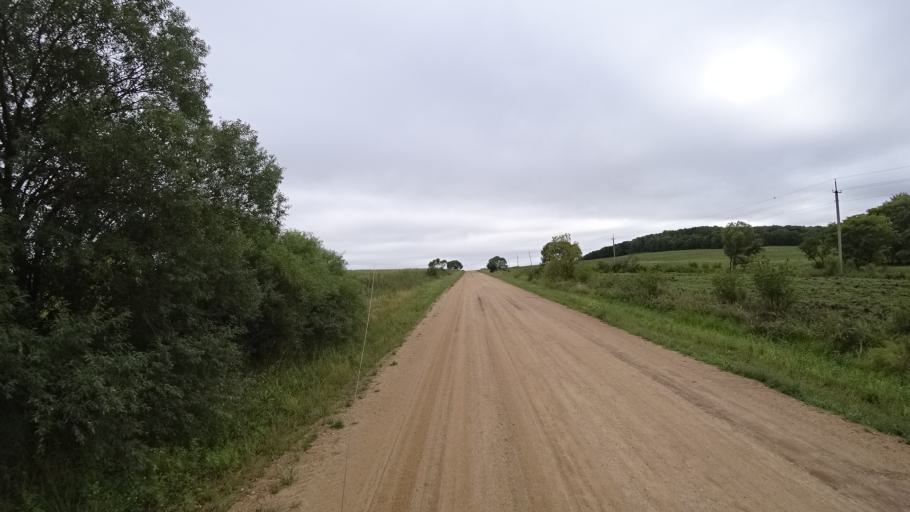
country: RU
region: Primorskiy
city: Monastyrishche
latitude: 44.0938
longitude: 132.6001
